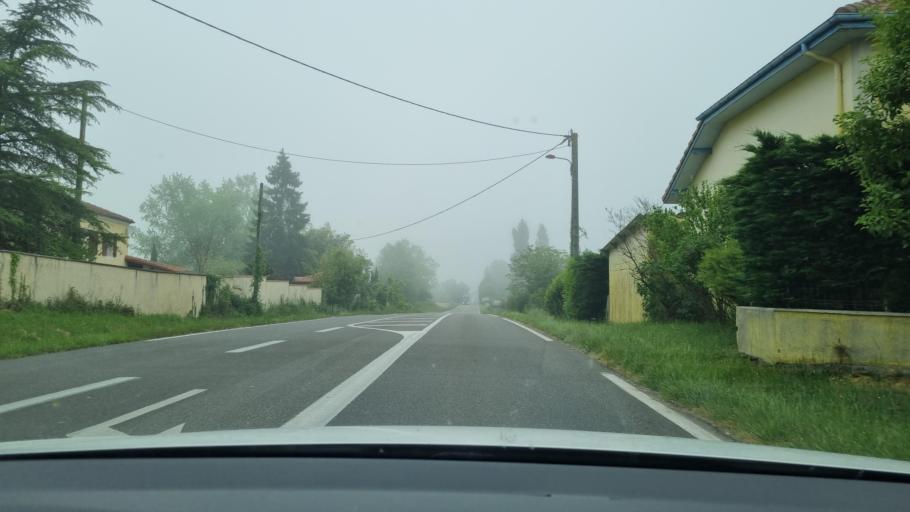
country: FR
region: Aquitaine
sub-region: Departement des Landes
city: Amou
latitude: 43.5847
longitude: -0.6535
